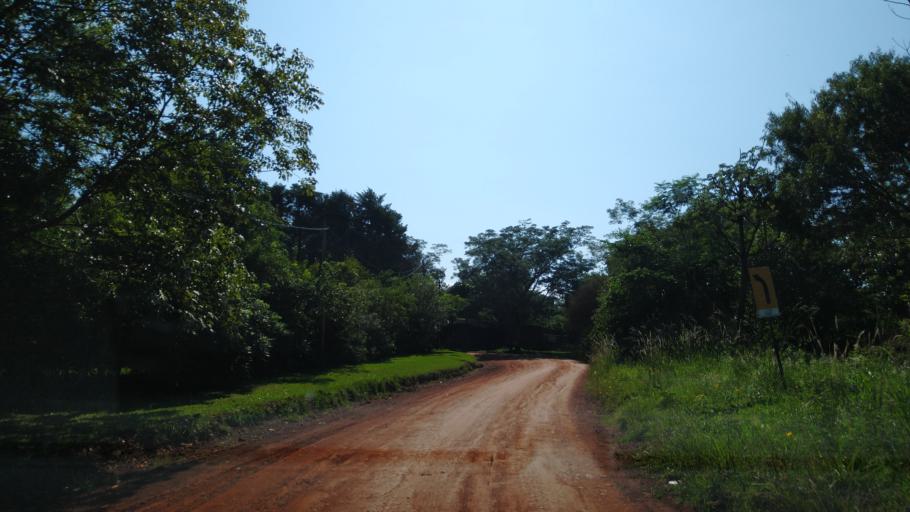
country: AR
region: Misiones
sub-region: Departamento de Capital
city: Posadas
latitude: -27.4072
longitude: -55.9770
